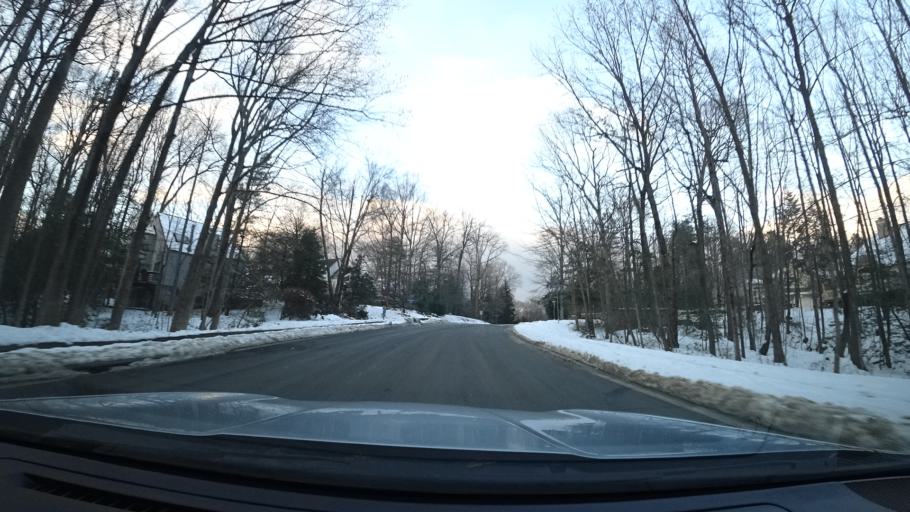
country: US
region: Virginia
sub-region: Fairfax County
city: Reston
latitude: 38.9783
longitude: -77.3448
